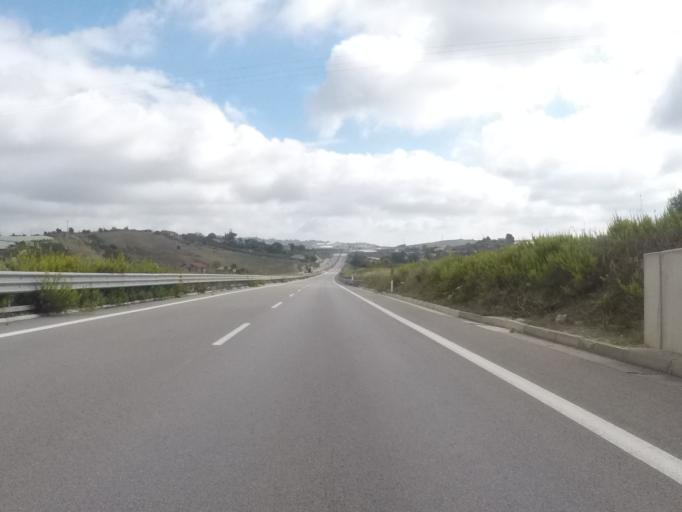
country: IT
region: Sicily
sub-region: Agrigento
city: Canicatti
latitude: 37.3929
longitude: 13.8431
